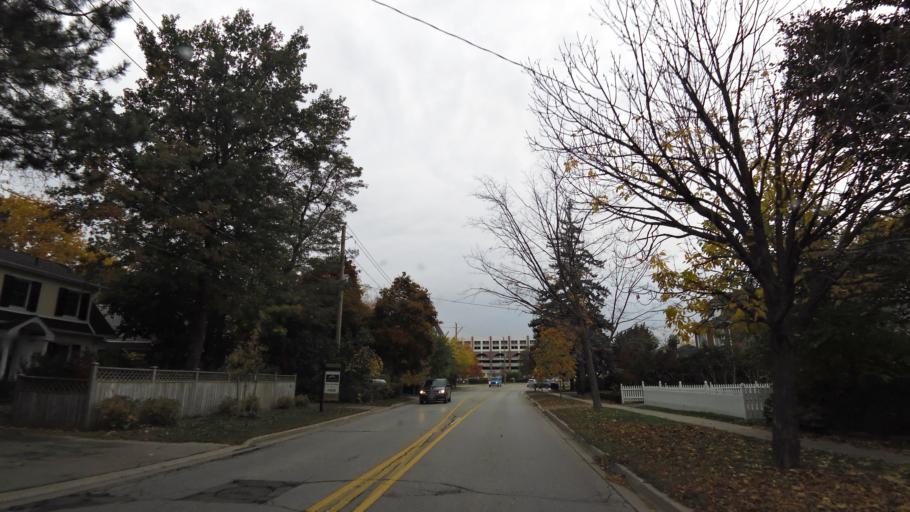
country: CA
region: Ontario
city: Oakville
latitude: 43.4535
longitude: -79.6786
